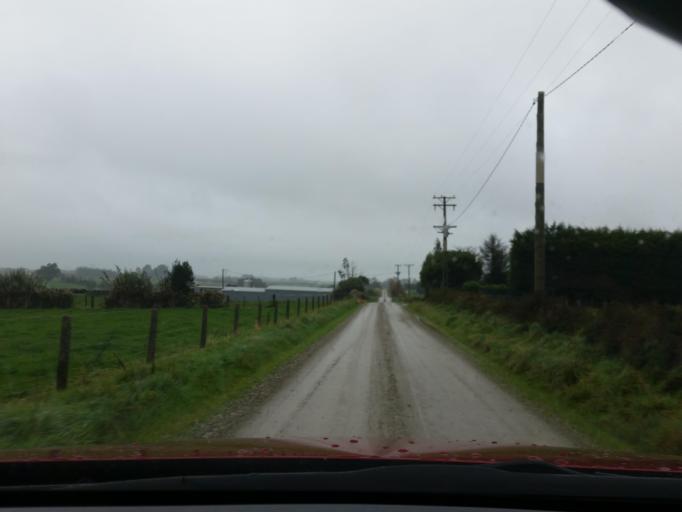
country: NZ
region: Southland
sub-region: Invercargill City
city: Invercargill
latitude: -46.3310
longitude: 168.4361
